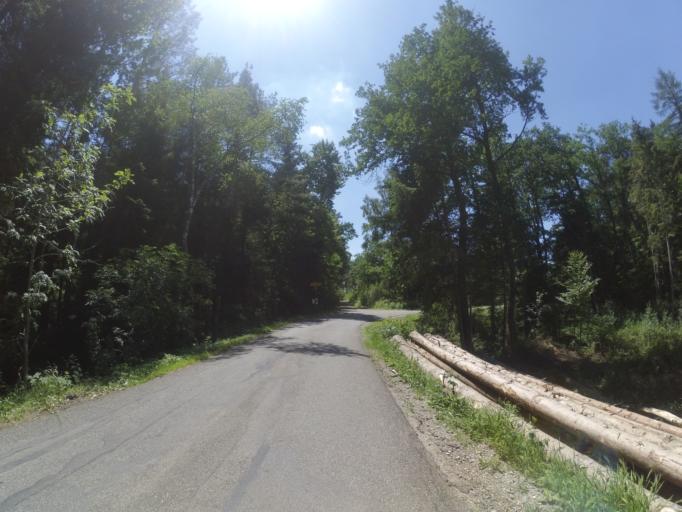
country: DE
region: Baden-Wuerttemberg
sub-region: Tuebingen Region
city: Bad Waldsee
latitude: 47.9194
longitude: 9.7191
